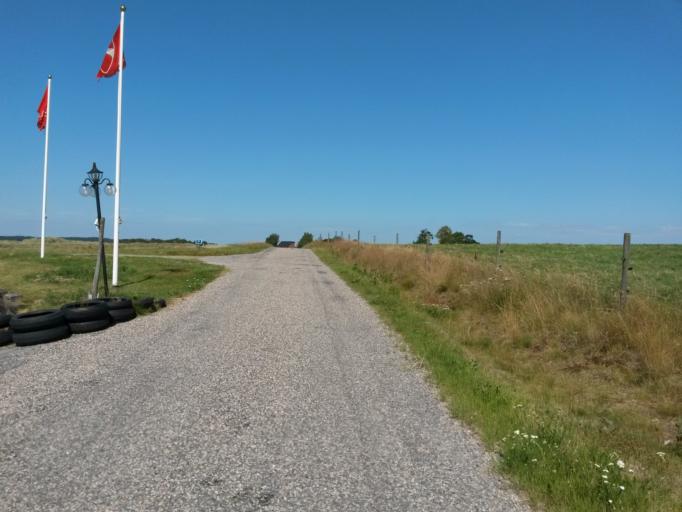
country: SE
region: Vaestra Goetaland
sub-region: Vargarda Kommun
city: Jonstorp
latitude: 57.9794
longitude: 12.6499
